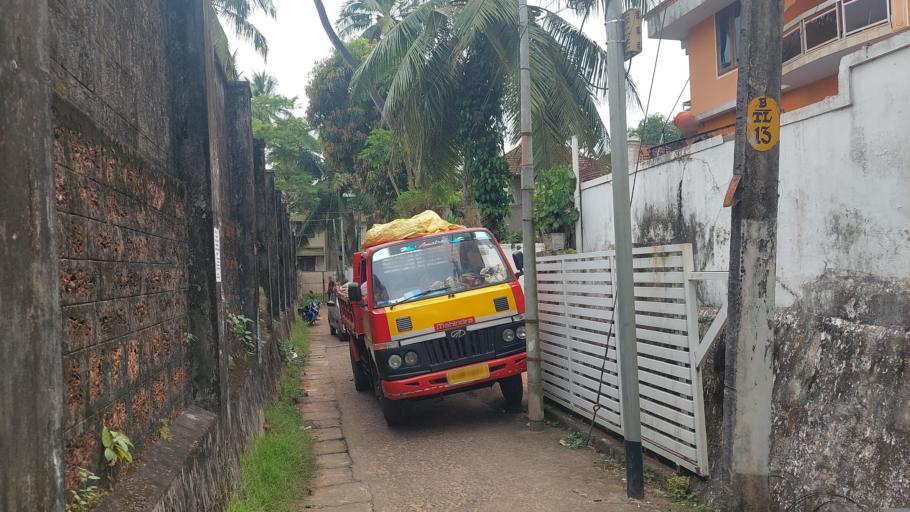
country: IN
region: Kerala
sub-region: Kozhikode
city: Kozhikode
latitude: 11.2463
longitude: 75.7780
